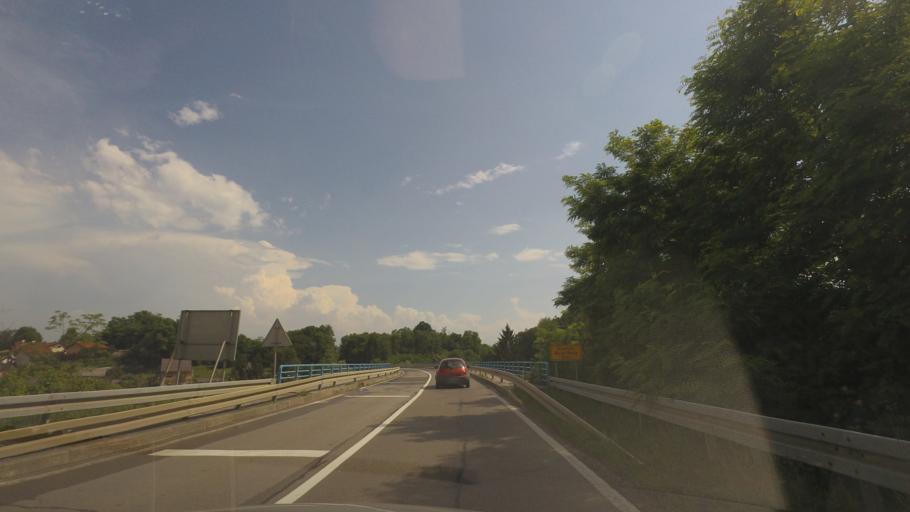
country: HR
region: Karlovacka
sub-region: Grad Karlovac
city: Karlovac
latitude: 45.4437
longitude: 15.4937
